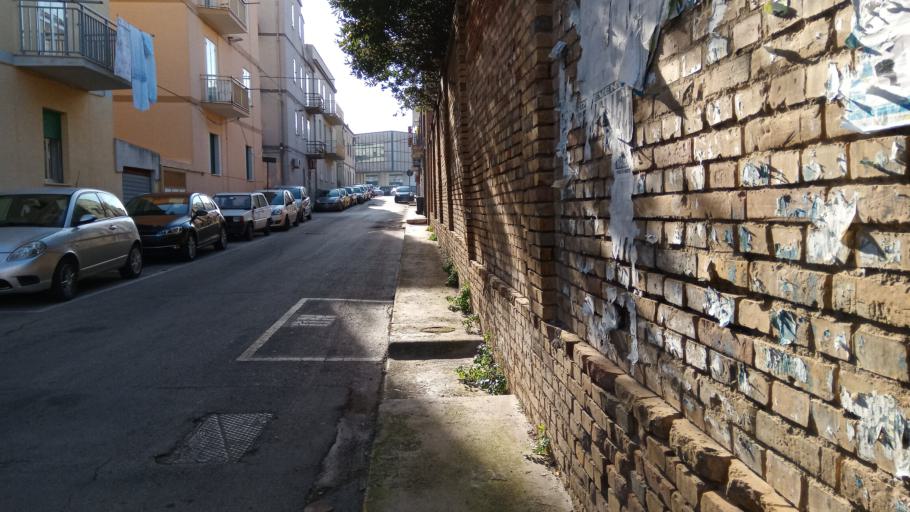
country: IT
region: Molise
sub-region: Provincia di Campobasso
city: Termoli
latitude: 42.0031
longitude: 14.9920
